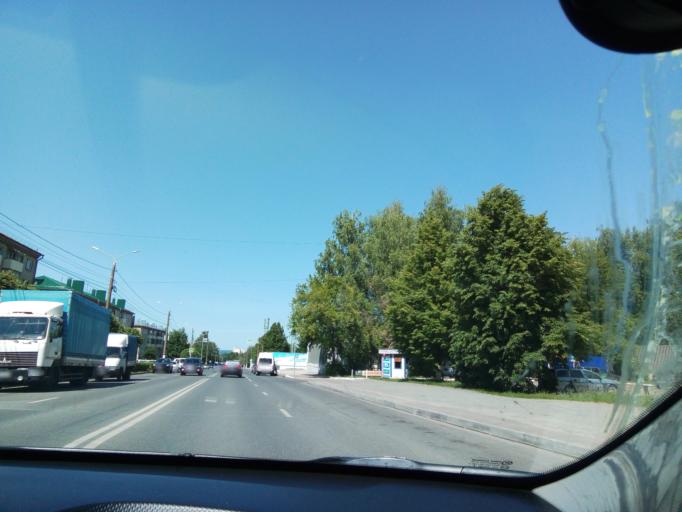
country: RU
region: Chuvashia
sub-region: Cheboksarskiy Rayon
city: Cheboksary
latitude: 56.1210
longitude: 47.2652
